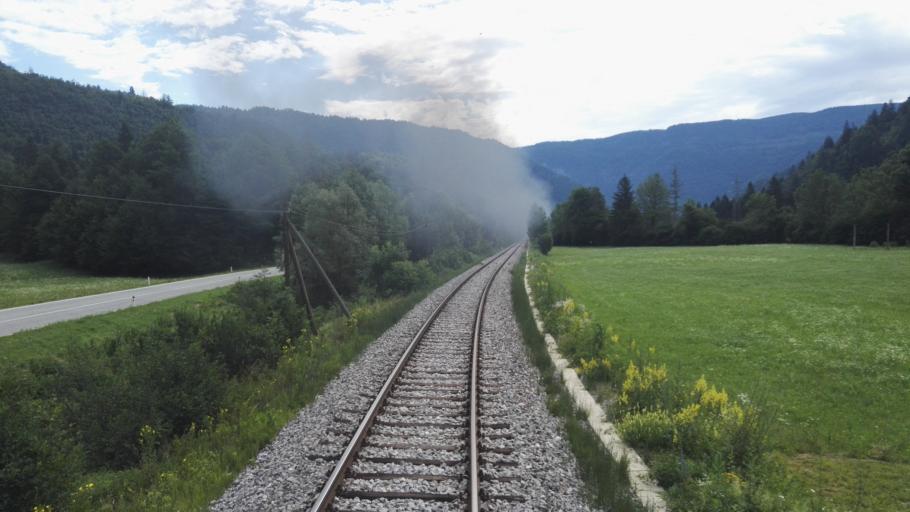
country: SI
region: Bohinj
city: Bohinjska Bistrica
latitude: 46.2876
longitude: 13.9811
